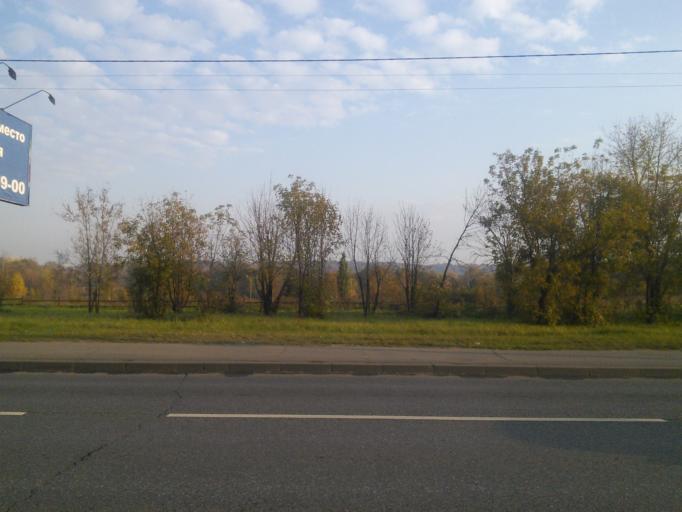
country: RU
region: Moskovskaya
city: Fili
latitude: 55.7570
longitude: 37.4629
